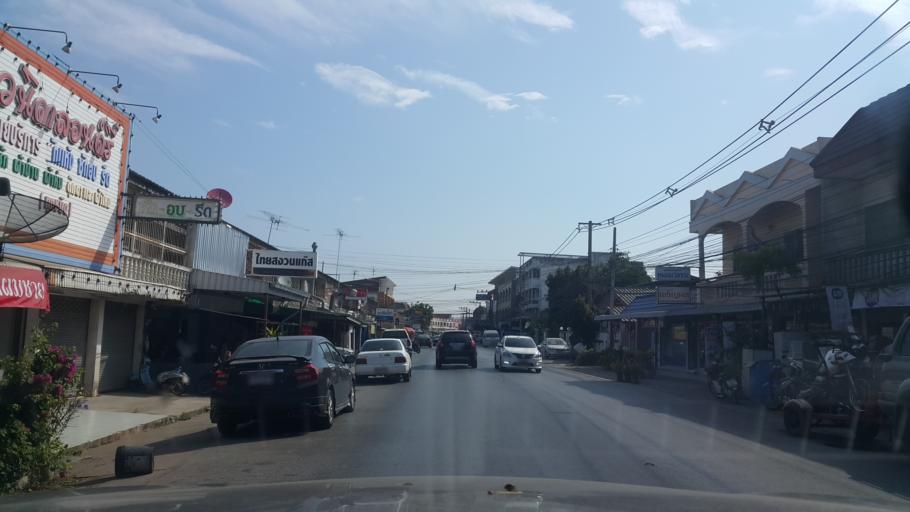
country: TH
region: Nakhon Ratchasima
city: Nakhon Ratchasima
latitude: 14.9490
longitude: 102.0450
